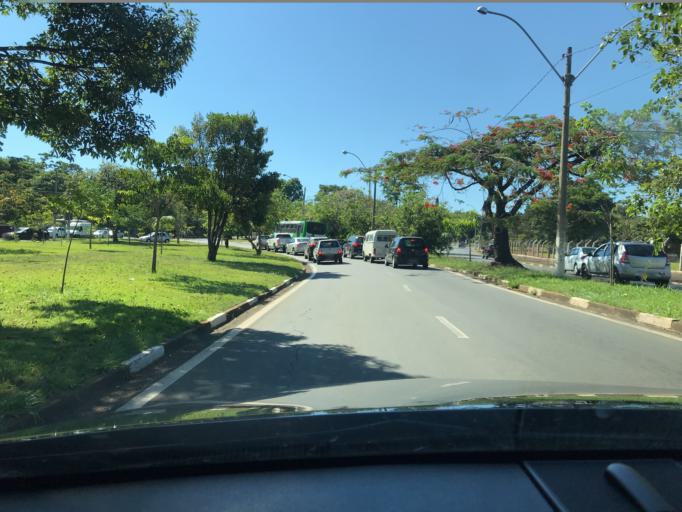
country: BR
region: Sao Paulo
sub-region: Campinas
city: Campinas
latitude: -22.8769
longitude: -47.0764
